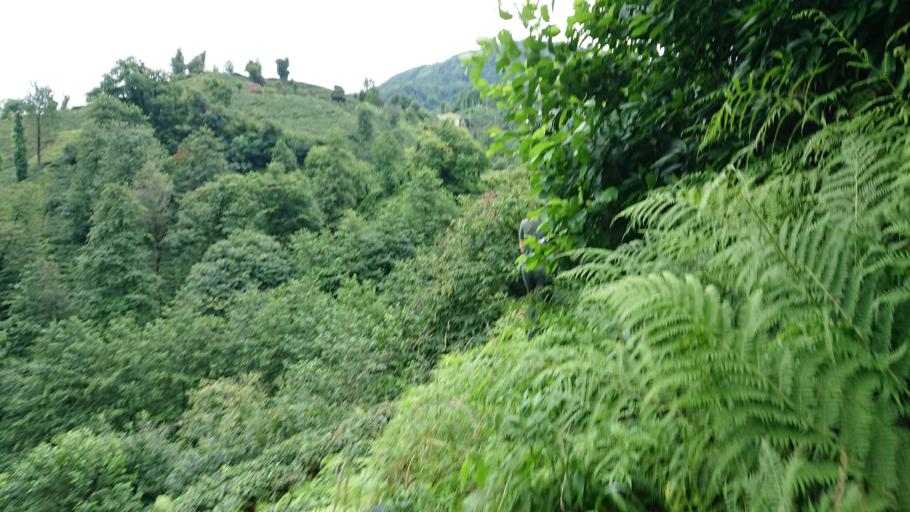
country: TR
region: Rize
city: Rize
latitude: 40.9851
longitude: 40.4872
